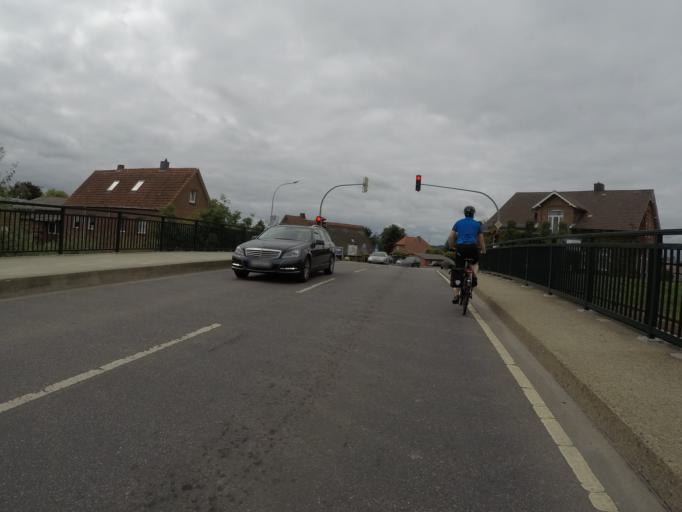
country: DE
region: Lower Saxony
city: Guderhandviertel
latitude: 53.5442
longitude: 9.6122
